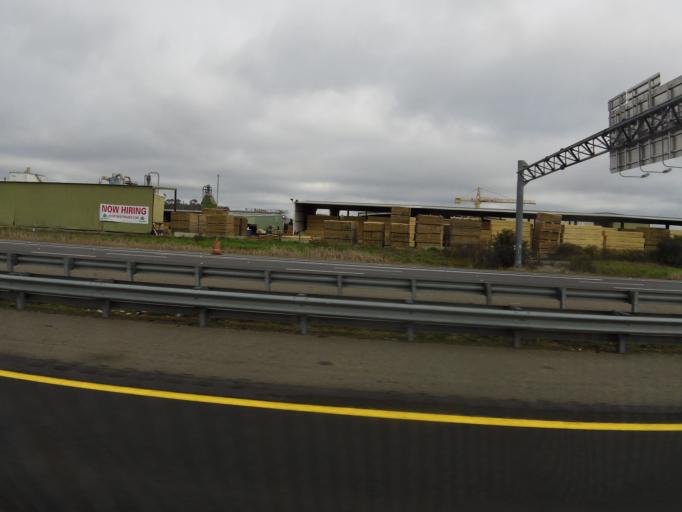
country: US
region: Florida
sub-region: Duval County
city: Baldwin
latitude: 30.3075
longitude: -81.8684
